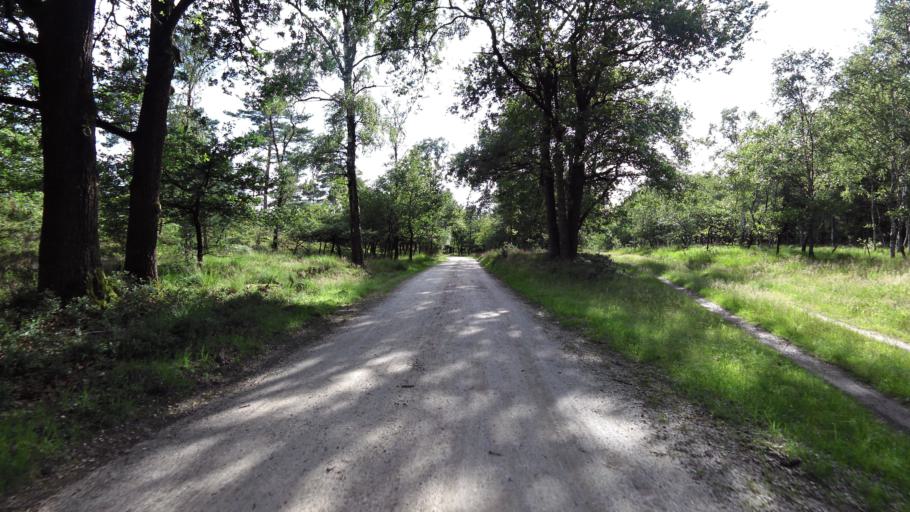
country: NL
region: Gelderland
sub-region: Gemeente Apeldoorn
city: Uddel
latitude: 52.2712
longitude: 5.8598
